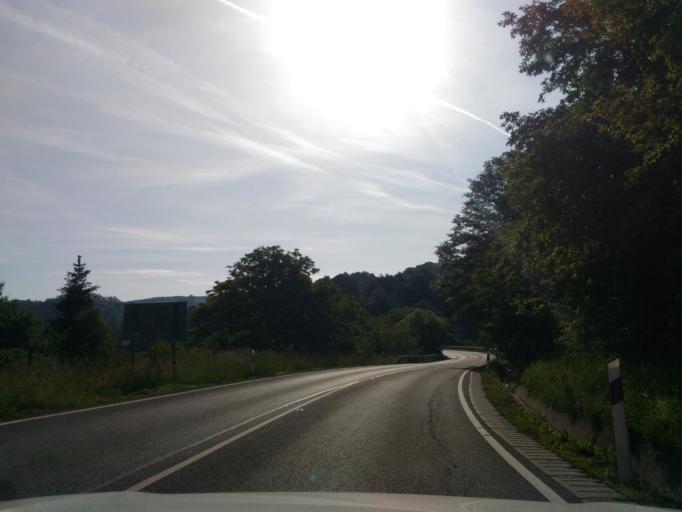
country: HU
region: Baranya
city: Komlo
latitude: 46.1599
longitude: 18.2436
